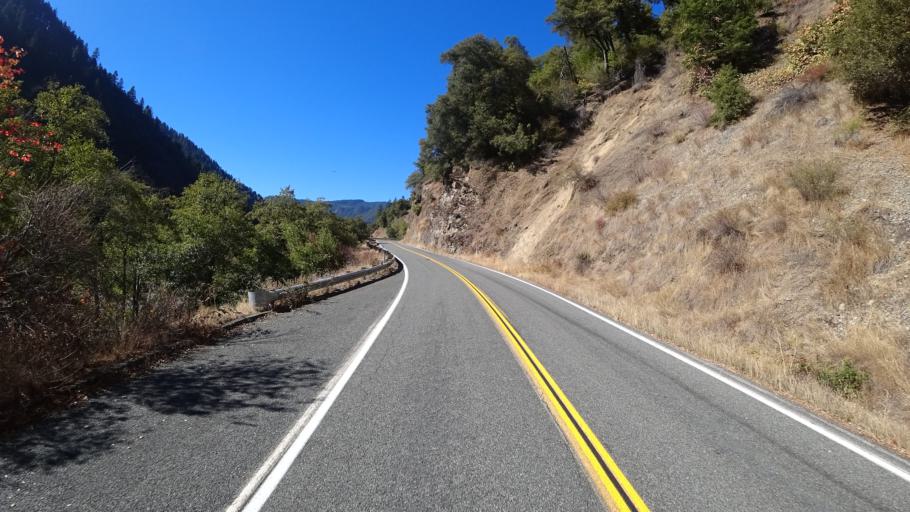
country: US
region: California
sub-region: Siskiyou County
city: Happy Camp
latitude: 41.3805
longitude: -123.4656
